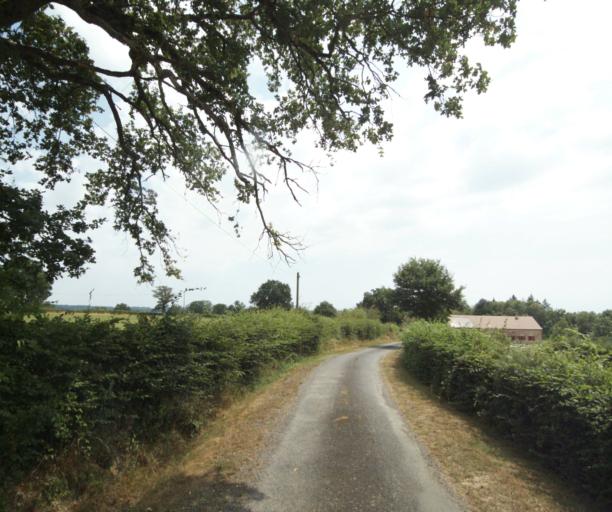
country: FR
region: Bourgogne
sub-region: Departement de Saone-et-Loire
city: Gueugnon
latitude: 46.5830
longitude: 4.0280
